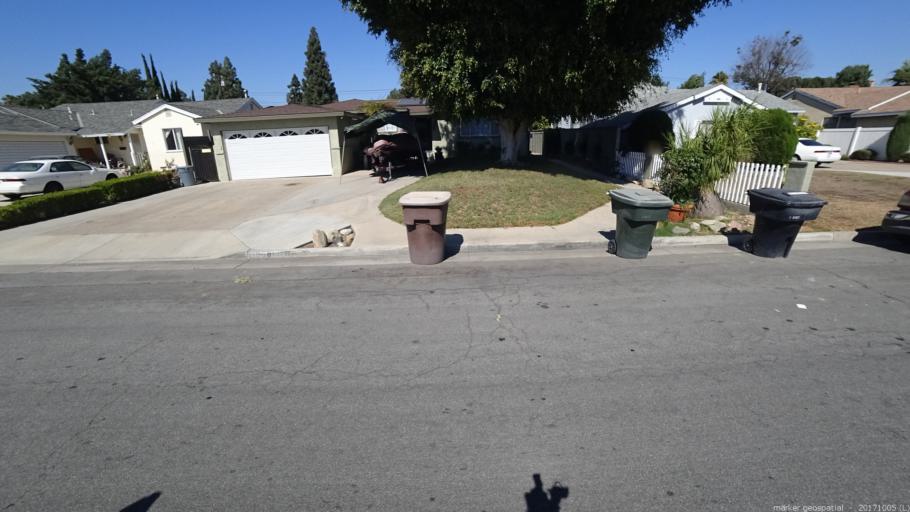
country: US
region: California
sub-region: Orange County
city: Garden Grove
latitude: 33.7863
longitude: -117.9643
